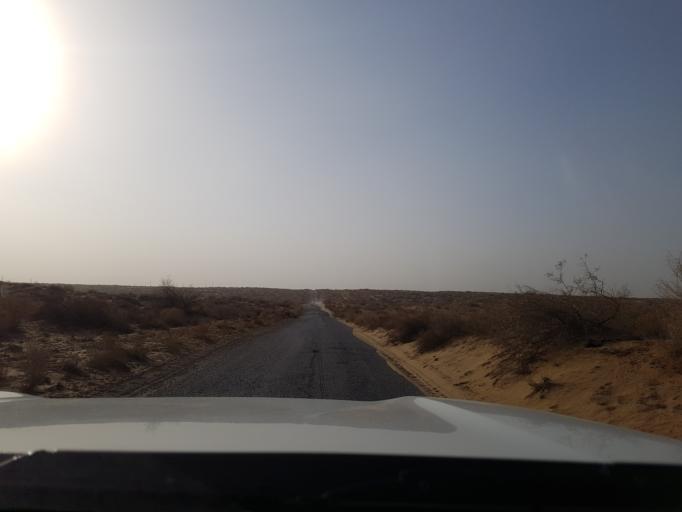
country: UZ
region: Xorazm
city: Hazorasp
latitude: 41.1943
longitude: 60.9170
